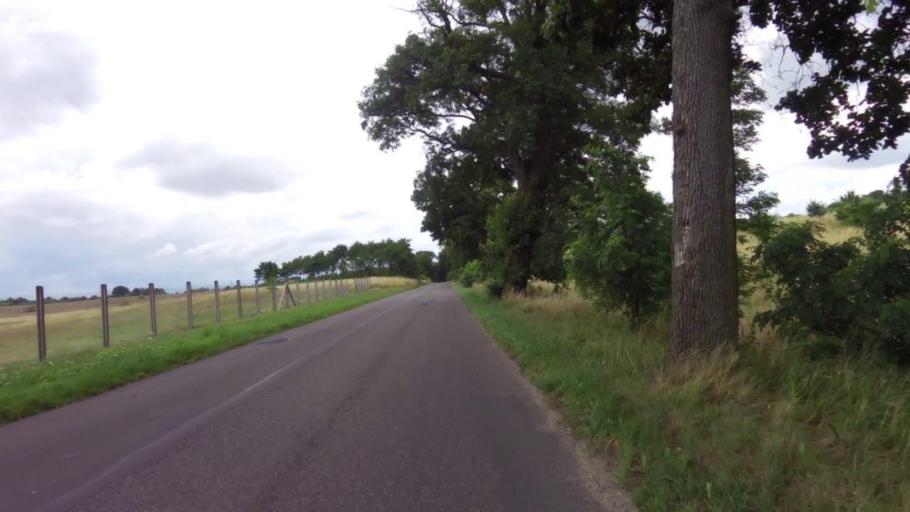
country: PL
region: West Pomeranian Voivodeship
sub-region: Powiat gryfinski
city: Moryn
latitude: 52.8640
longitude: 14.3862
